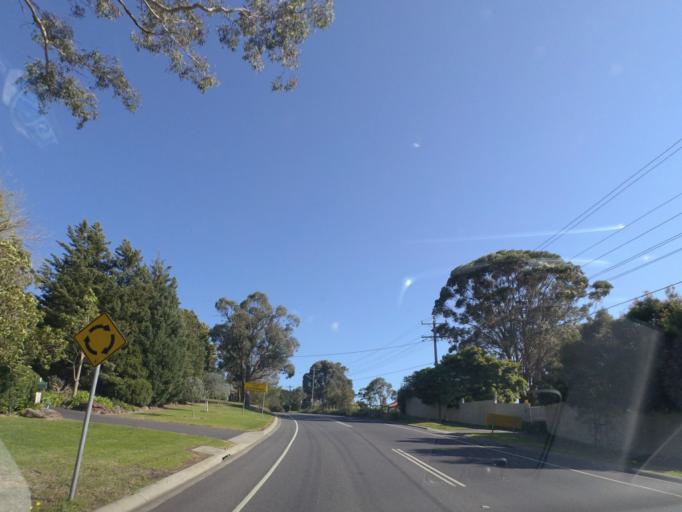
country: AU
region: Victoria
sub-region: Manningham
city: Donvale
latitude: -37.7775
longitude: 145.1861
